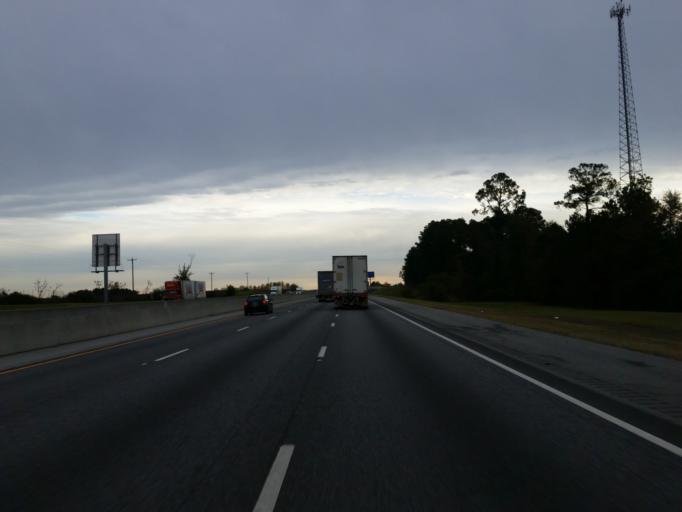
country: US
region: Georgia
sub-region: Turner County
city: Ashburn
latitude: 31.6516
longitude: -83.5966
